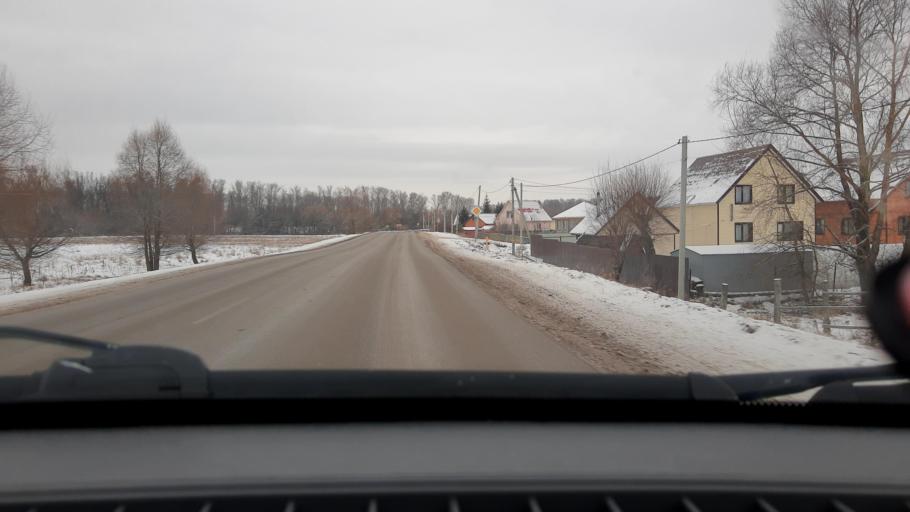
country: RU
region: Bashkortostan
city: Iglino
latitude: 54.8451
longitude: 56.4527
